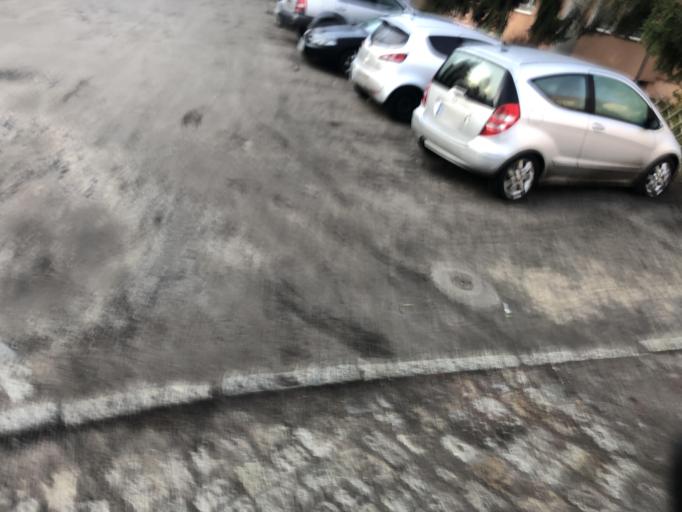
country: DE
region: Berlin
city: Frohnau
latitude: 52.6257
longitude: 13.2805
